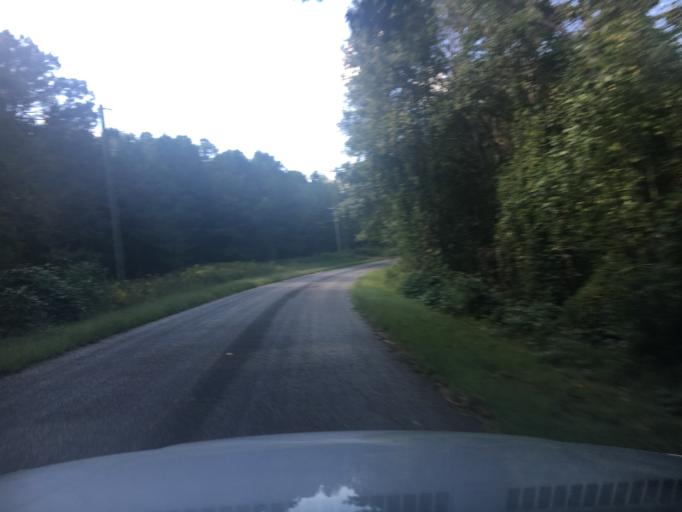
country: US
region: South Carolina
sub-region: Greenwood County
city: Ware Shoals
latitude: 34.4949
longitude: -82.2330
